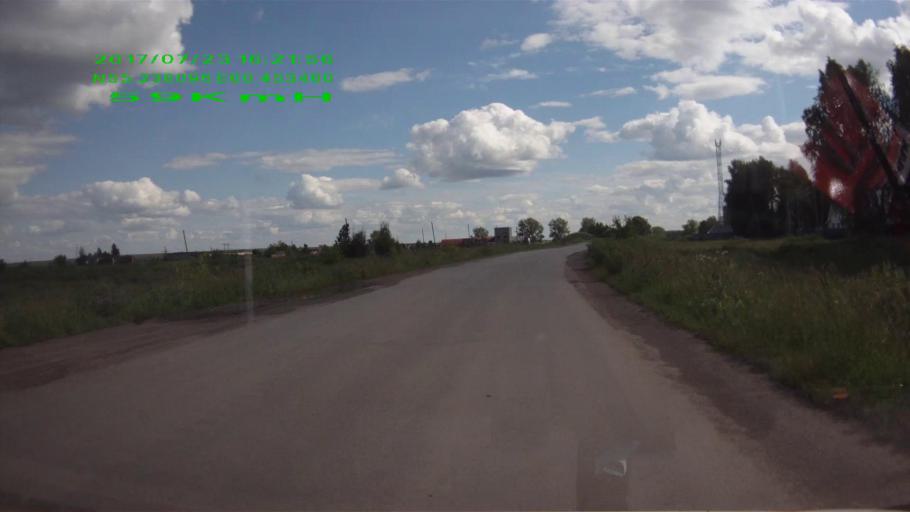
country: RU
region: Chelyabinsk
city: Chebarkul'
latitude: 55.2360
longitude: 60.4536
